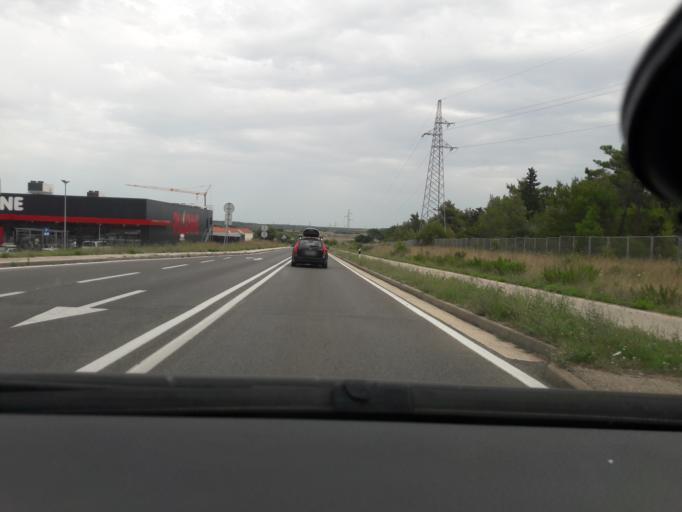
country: HR
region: Zadarska
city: Nin
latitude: 44.2389
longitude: 15.1726
